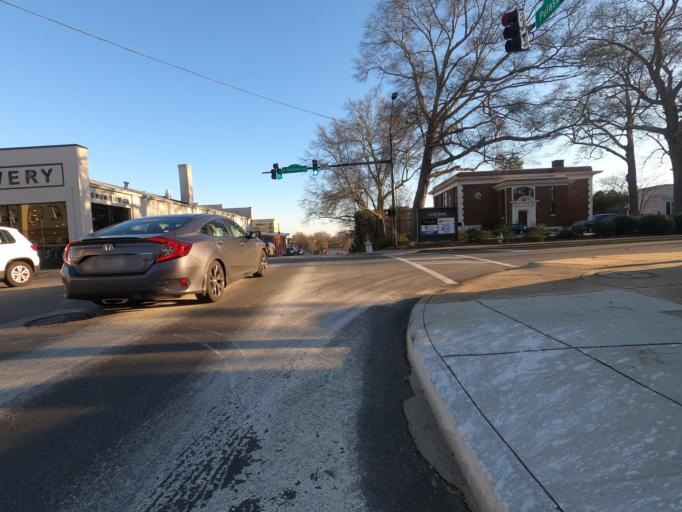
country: US
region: Georgia
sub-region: Clarke County
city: Athens
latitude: 33.9592
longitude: -83.3807
